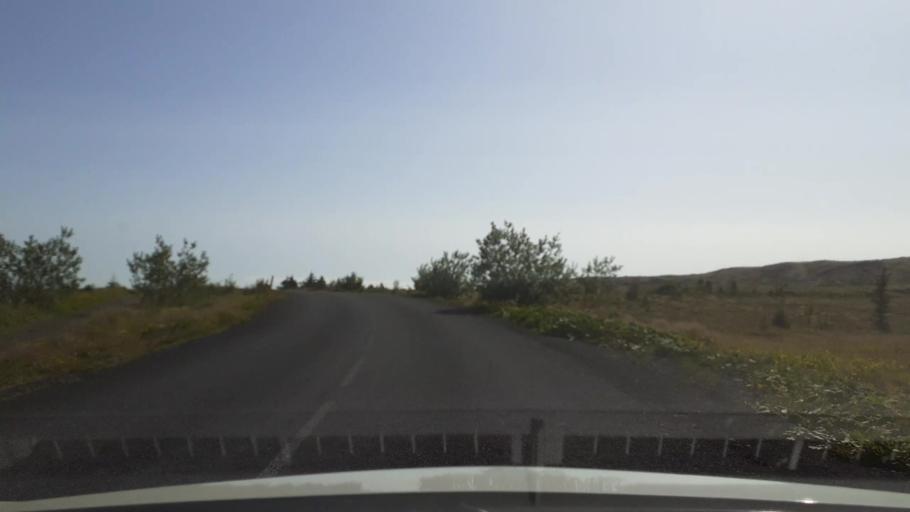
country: IS
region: South
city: Hveragerdi
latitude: 64.0166
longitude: -21.2108
